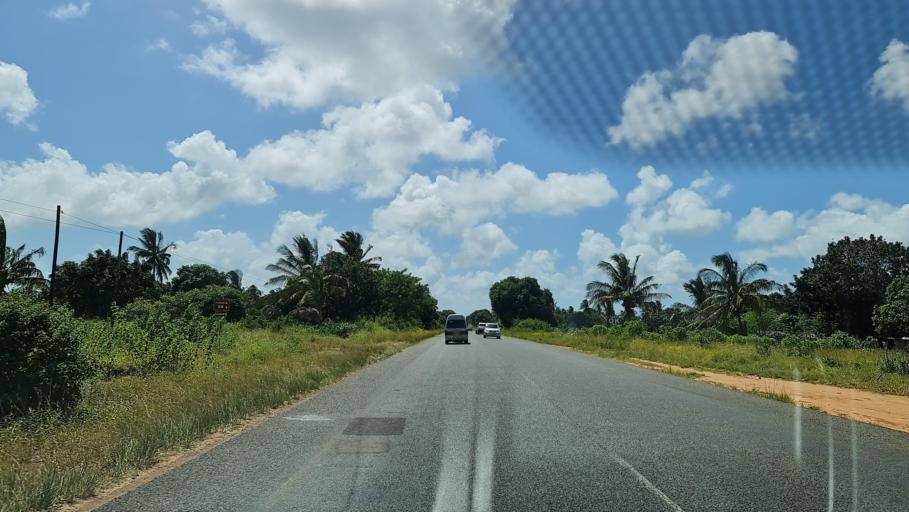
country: MZ
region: Inhambane
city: Maxixe
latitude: -24.5410
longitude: 34.9176
